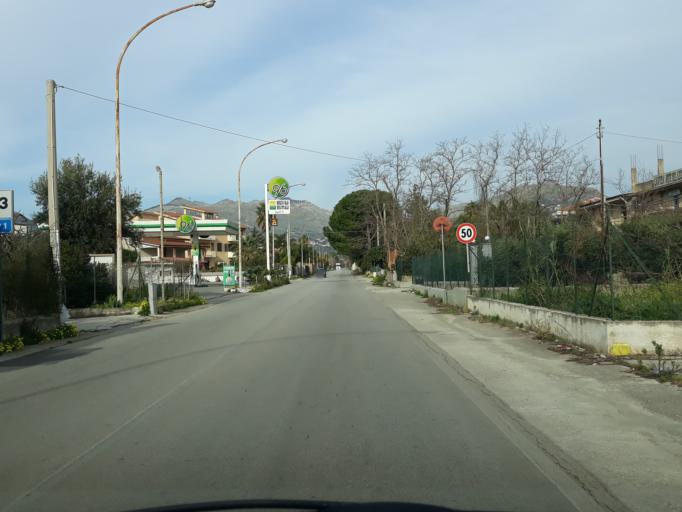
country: IT
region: Sicily
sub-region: Palermo
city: Borgetto
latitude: 38.0623
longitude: 13.1424
